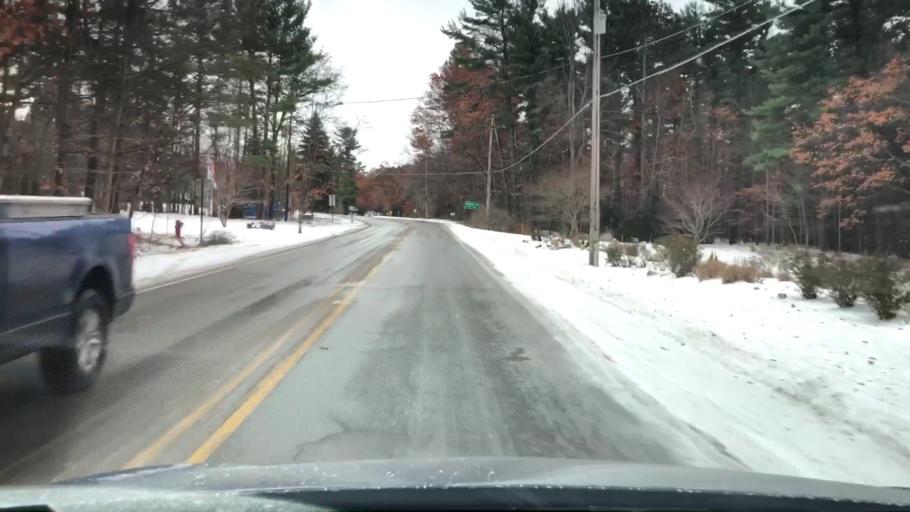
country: US
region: Michigan
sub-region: Grand Traverse County
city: Traverse City
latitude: 44.7753
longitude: -85.5911
